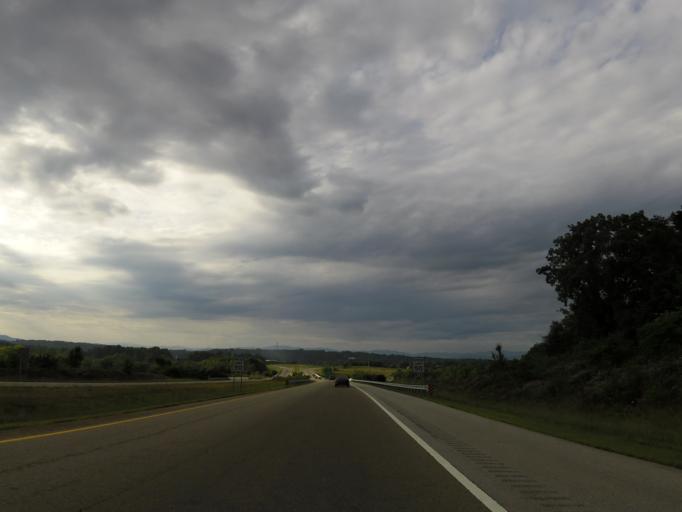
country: US
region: Tennessee
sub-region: Blount County
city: Eagleton Village
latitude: 35.8136
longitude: -83.9480
